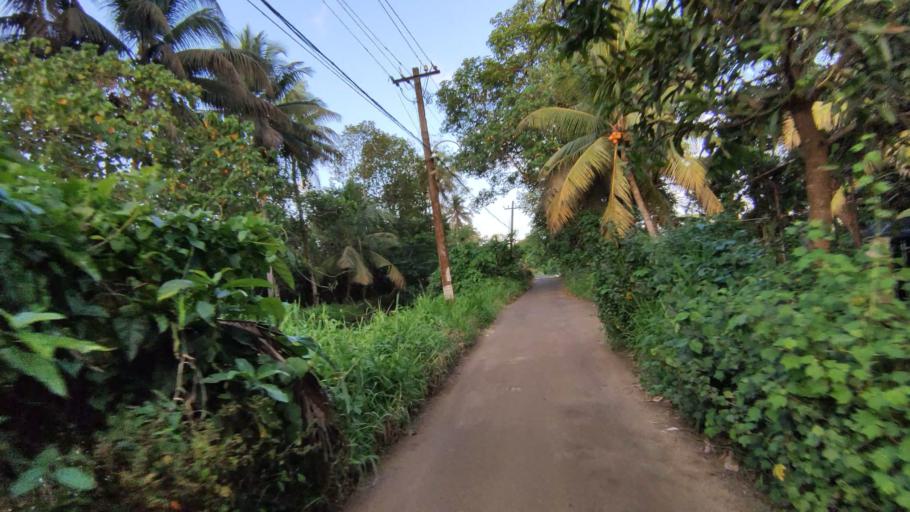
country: IN
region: Kerala
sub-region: Kottayam
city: Kottayam
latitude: 9.5951
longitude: 76.4559
